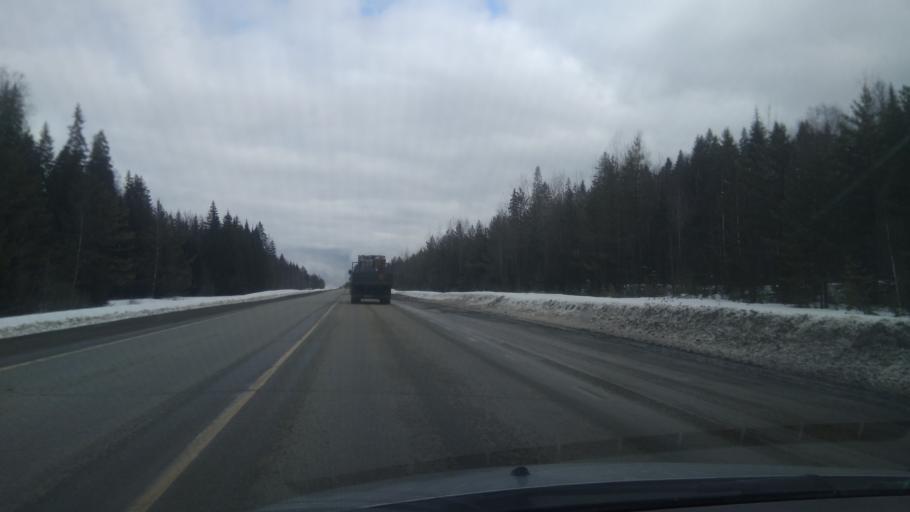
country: RU
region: Sverdlovsk
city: Nizhniye Sergi
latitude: 56.8257
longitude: 59.2312
